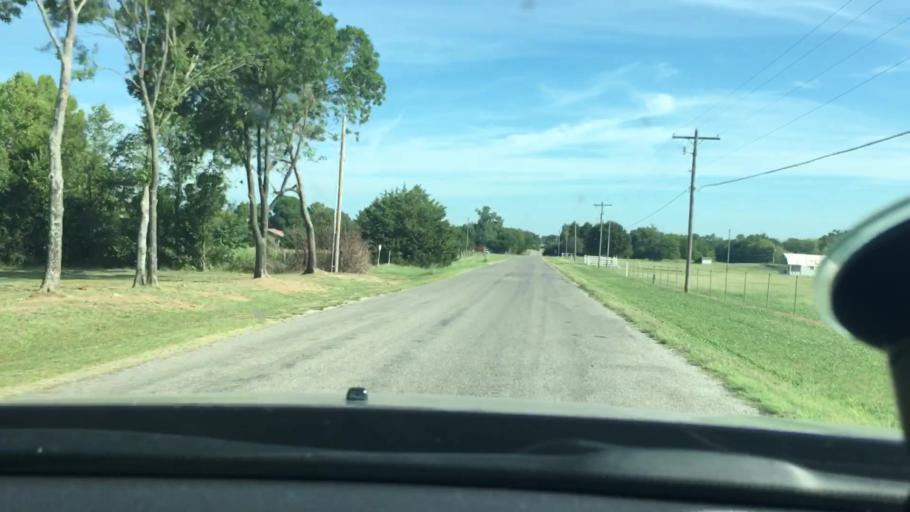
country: US
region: Oklahoma
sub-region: Carter County
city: Lone Grove
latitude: 34.2279
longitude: -97.2474
